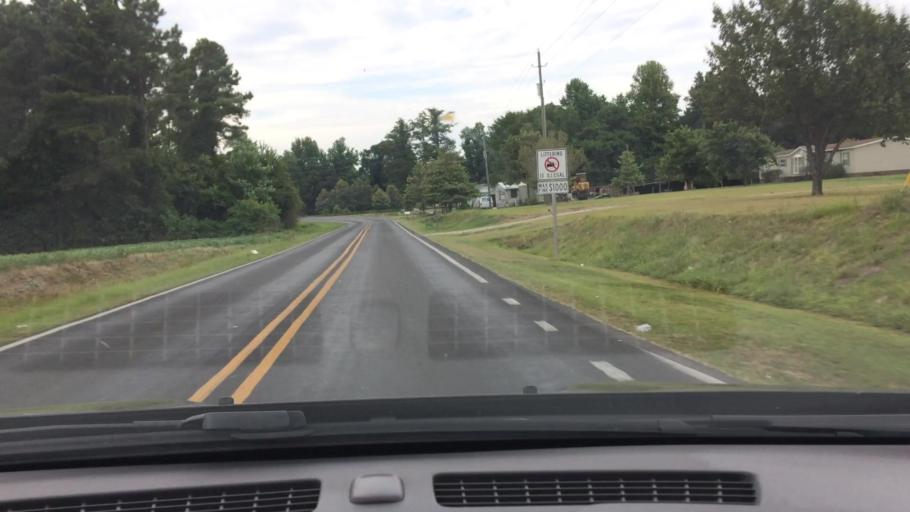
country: US
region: North Carolina
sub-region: Pitt County
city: Ayden
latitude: 35.4480
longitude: -77.4108
